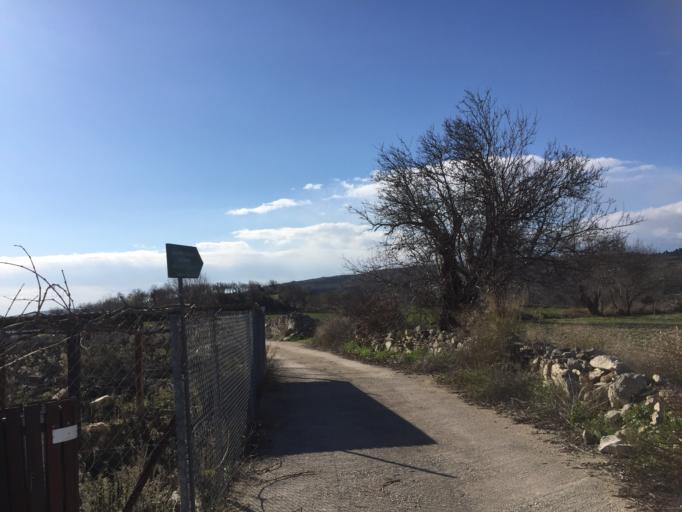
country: CY
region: Pafos
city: Mesogi
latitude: 34.8389
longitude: 32.5101
